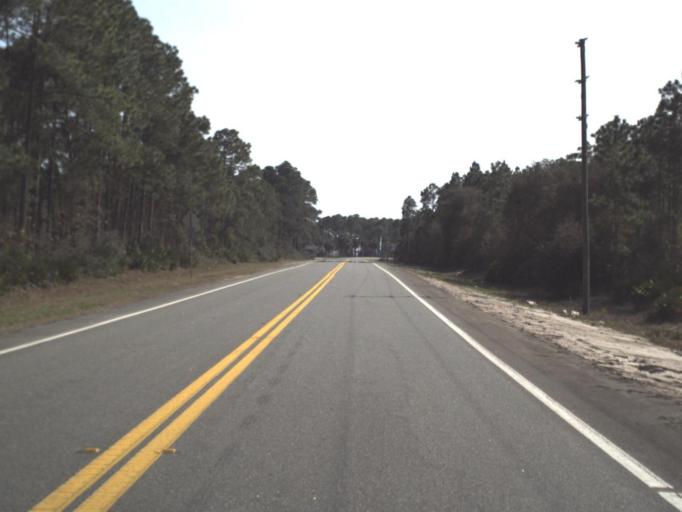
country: US
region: Florida
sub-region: Franklin County
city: Carrabelle
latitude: 29.9225
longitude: -84.5204
